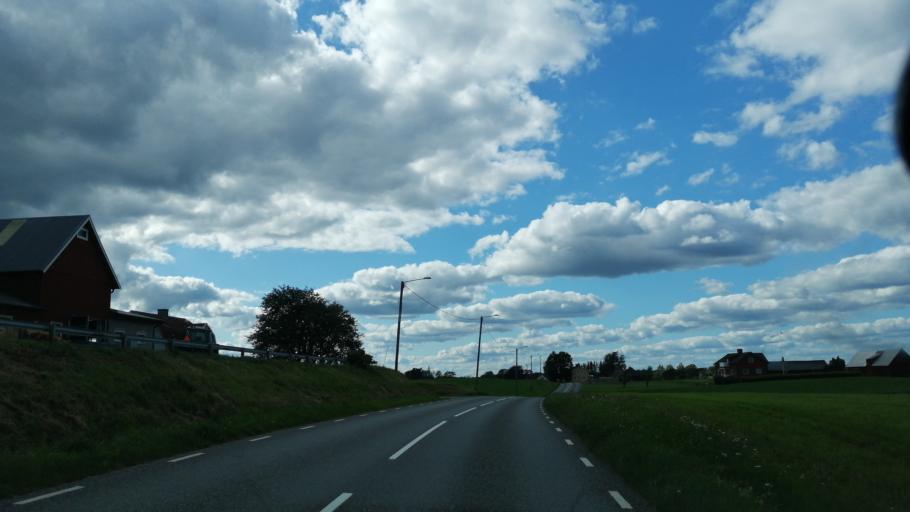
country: SE
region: Joenkoeping
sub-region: Gislaveds Kommun
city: Reftele
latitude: 57.1638
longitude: 13.6175
